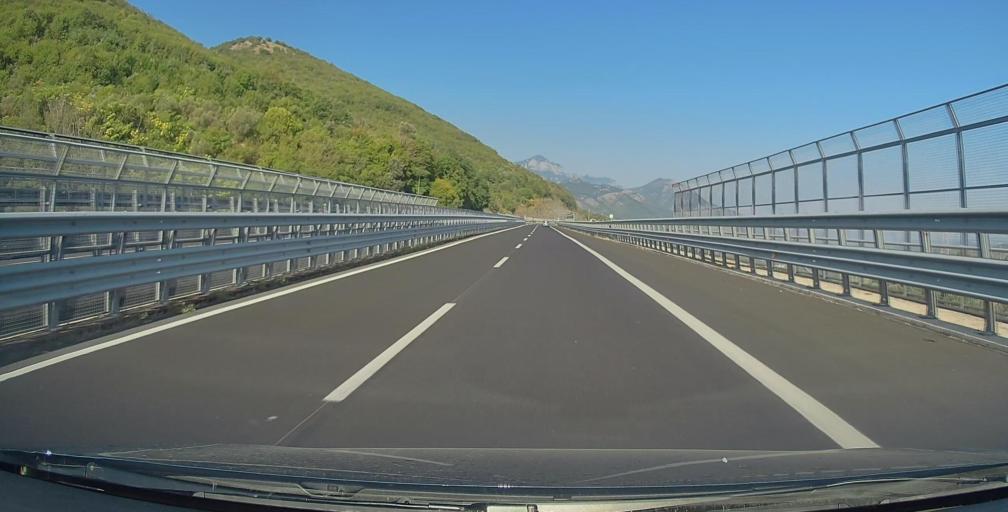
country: IT
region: Campania
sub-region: Provincia di Salerno
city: Polla
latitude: 40.5325
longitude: 15.4802
